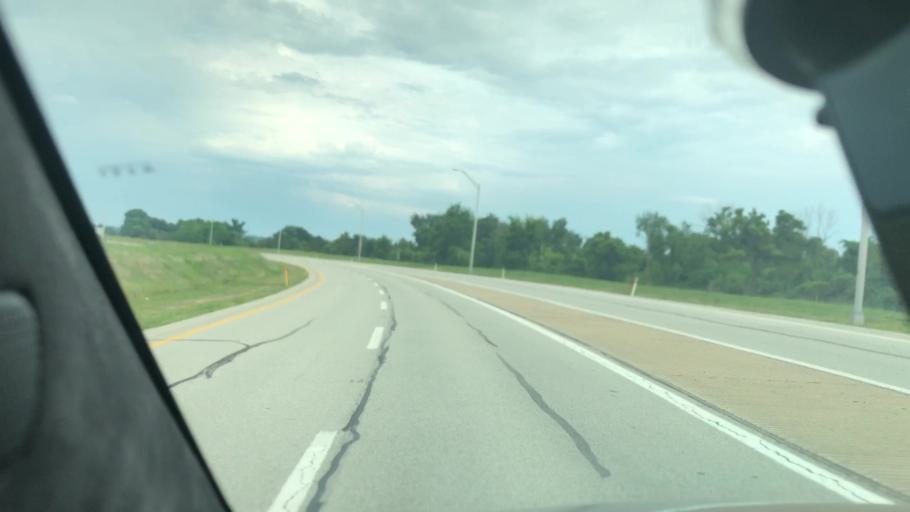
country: US
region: Pennsylvania
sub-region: Washington County
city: Baidland
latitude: 40.1879
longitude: -79.9891
